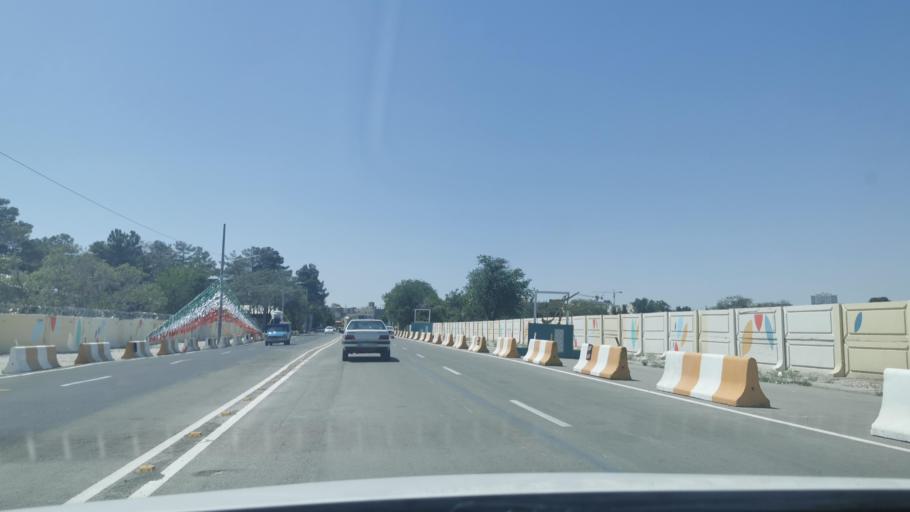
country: IR
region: Razavi Khorasan
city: Mashhad
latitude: 36.2743
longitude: 59.5813
